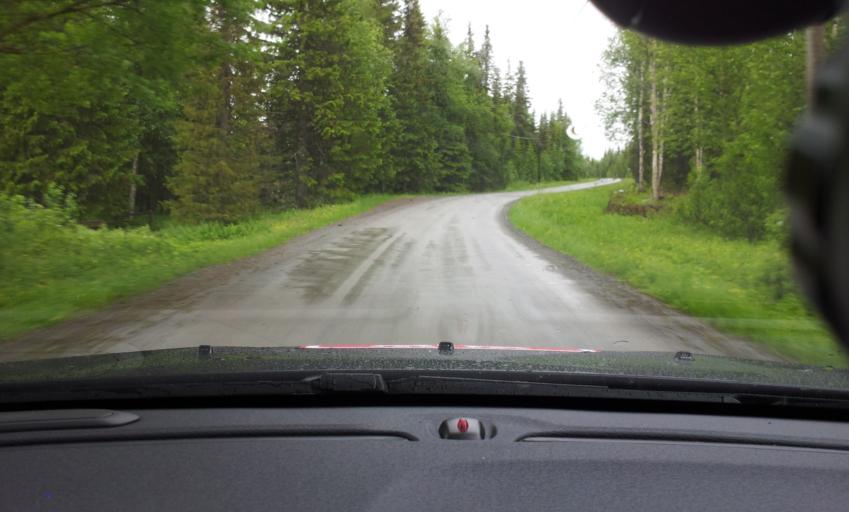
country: SE
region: Jaemtland
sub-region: Are Kommun
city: Are
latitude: 63.4292
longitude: 12.8035
